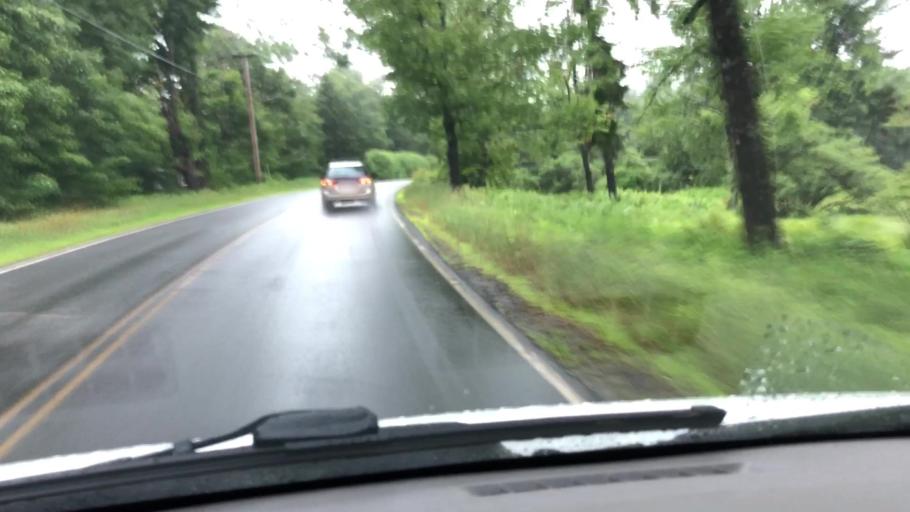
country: US
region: Massachusetts
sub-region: Hampshire County
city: Chesterfield
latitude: 42.4440
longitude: -72.9764
